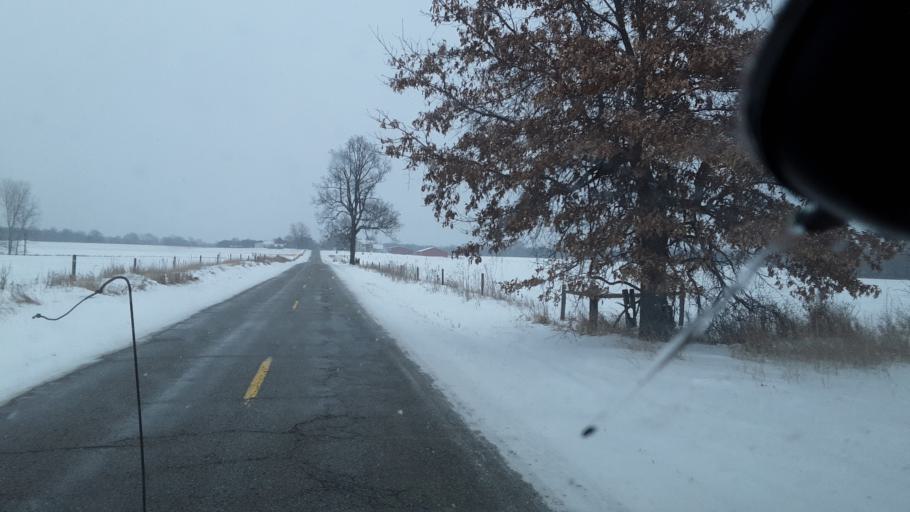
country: US
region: Michigan
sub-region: Ingham County
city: Leslie
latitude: 42.4897
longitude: -84.3271
